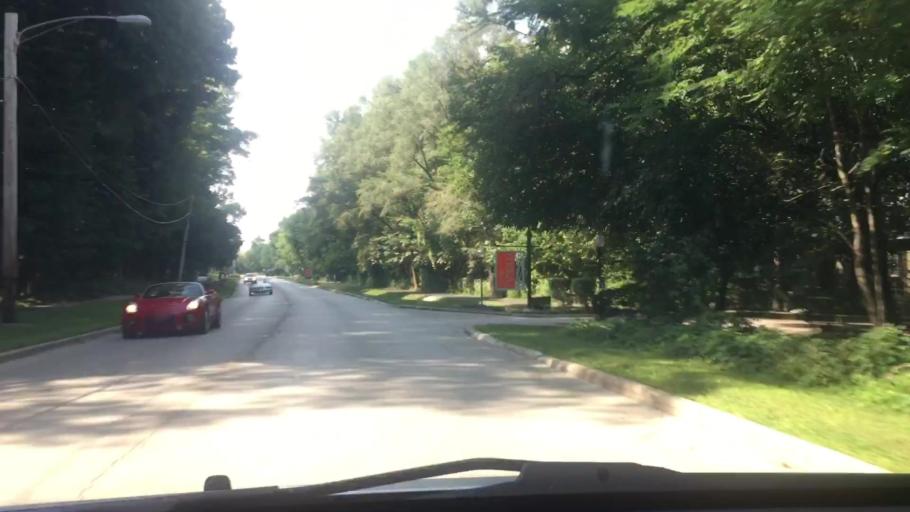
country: US
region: Illinois
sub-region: Kane County
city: Saint Charles
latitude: 41.9030
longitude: -88.3069
